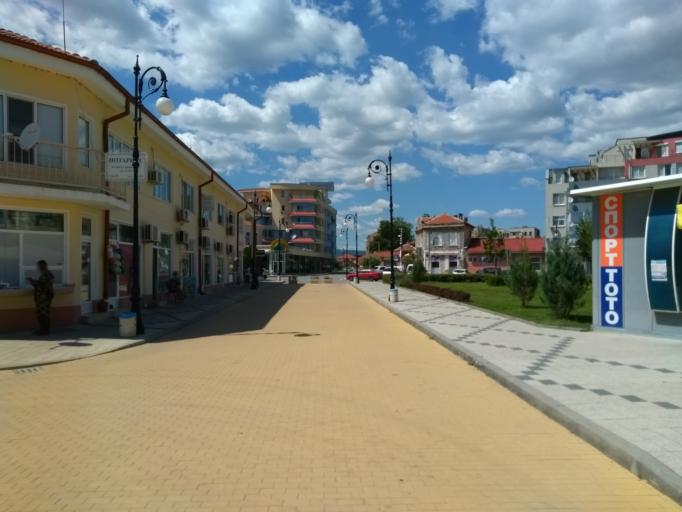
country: BG
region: Sliven
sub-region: Obshtina Nova Zagora
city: Nova Zagora
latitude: 42.4930
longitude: 26.0085
